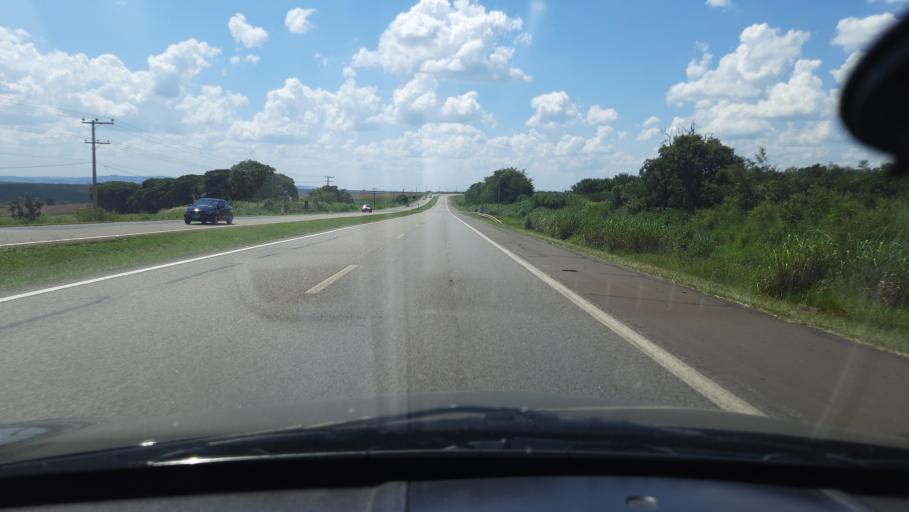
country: BR
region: Sao Paulo
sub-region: Casa Branca
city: Casa Branca
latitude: -21.7159
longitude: -47.0823
